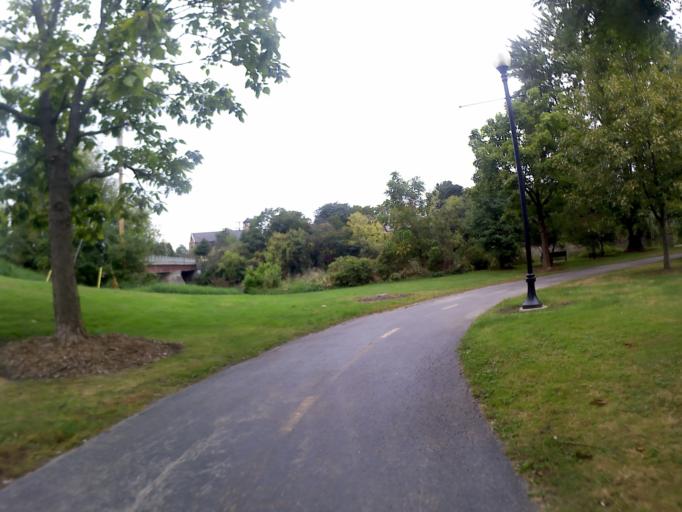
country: US
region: Illinois
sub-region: Kendall County
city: Oswego
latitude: 41.6850
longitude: -88.3554
